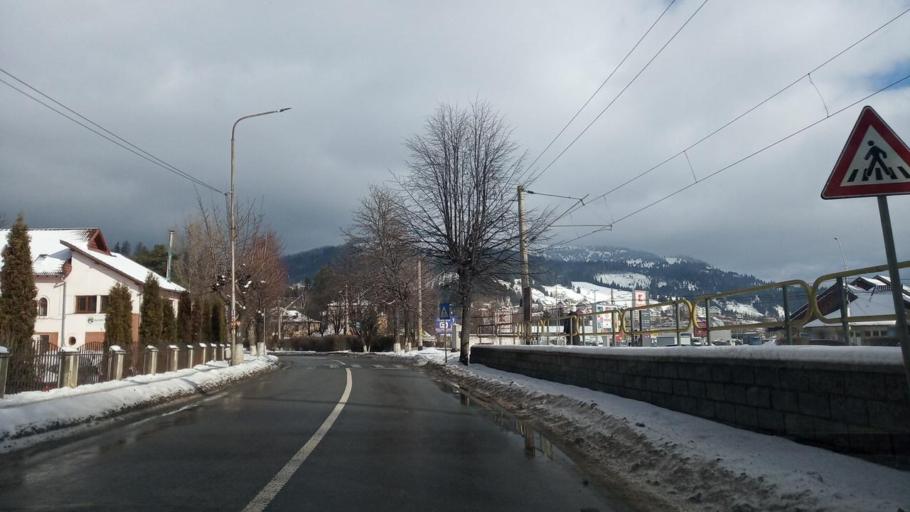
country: RO
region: Suceava
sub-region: Municipiul Vatra Dornei
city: Vatra Dornei
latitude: 47.3472
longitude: 25.3597
